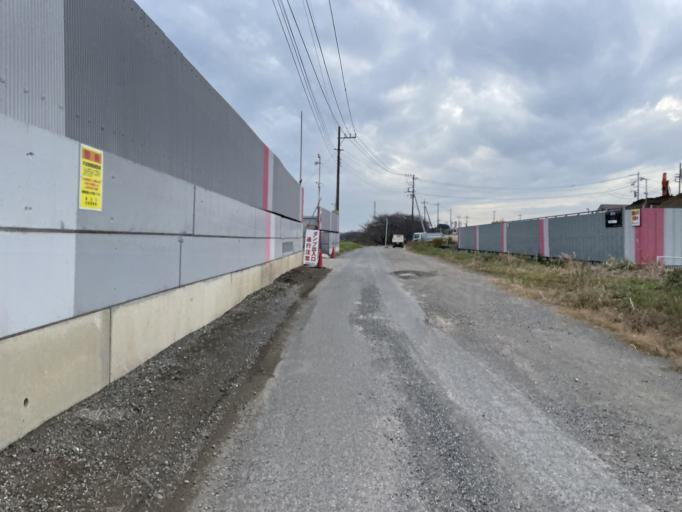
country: JP
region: Saitama
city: Shiraoka
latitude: 36.0074
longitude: 139.6496
